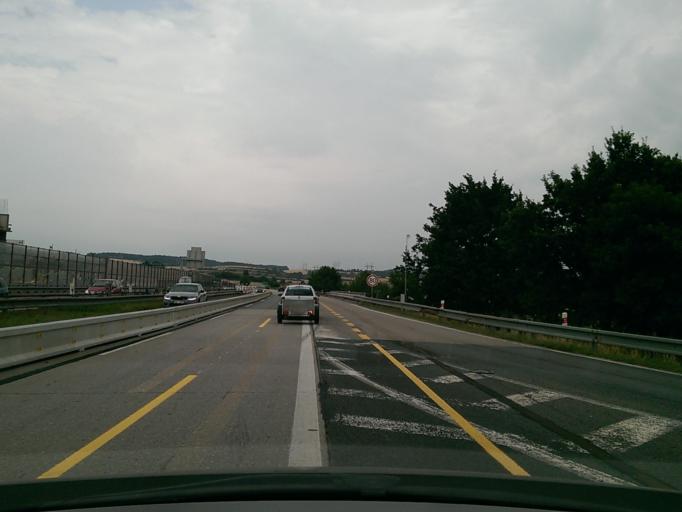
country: CZ
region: South Moravian
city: Ricany
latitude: 49.2156
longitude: 16.4115
